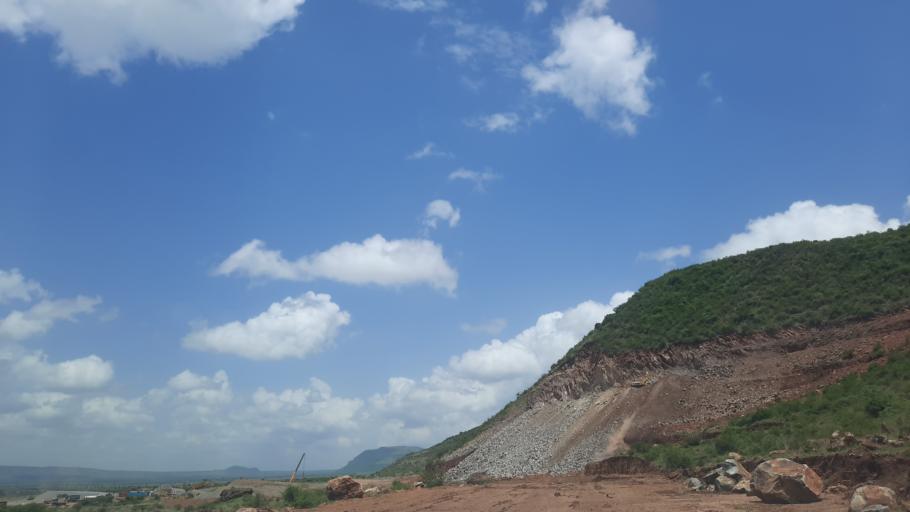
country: ET
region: Oromiya
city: Ziway
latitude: 7.9390
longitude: 38.6172
